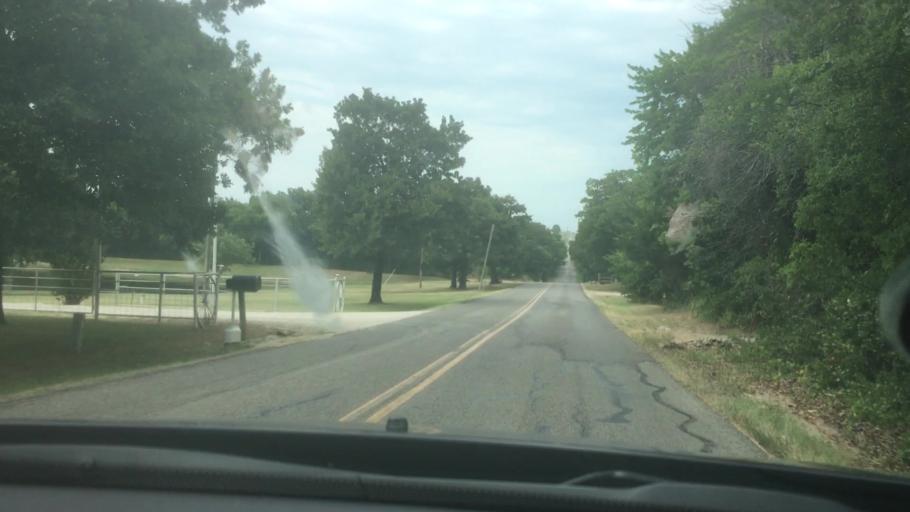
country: US
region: Oklahoma
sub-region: Murray County
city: Davis
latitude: 34.4933
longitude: -97.0555
